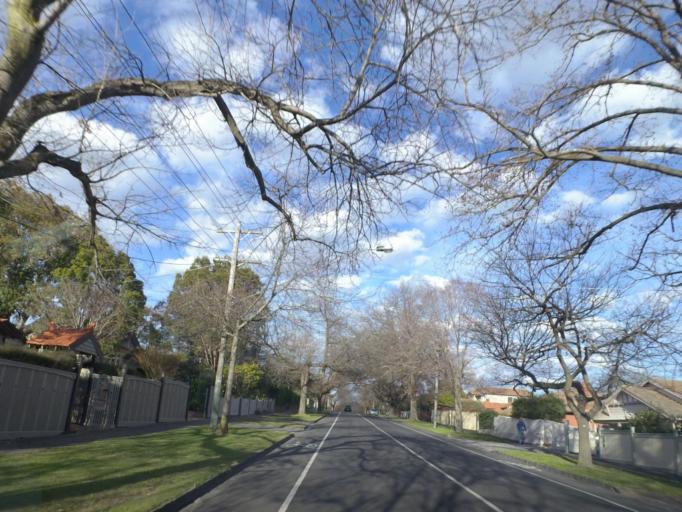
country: AU
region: Victoria
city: Mont Albert
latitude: -37.8198
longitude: 145.0929
